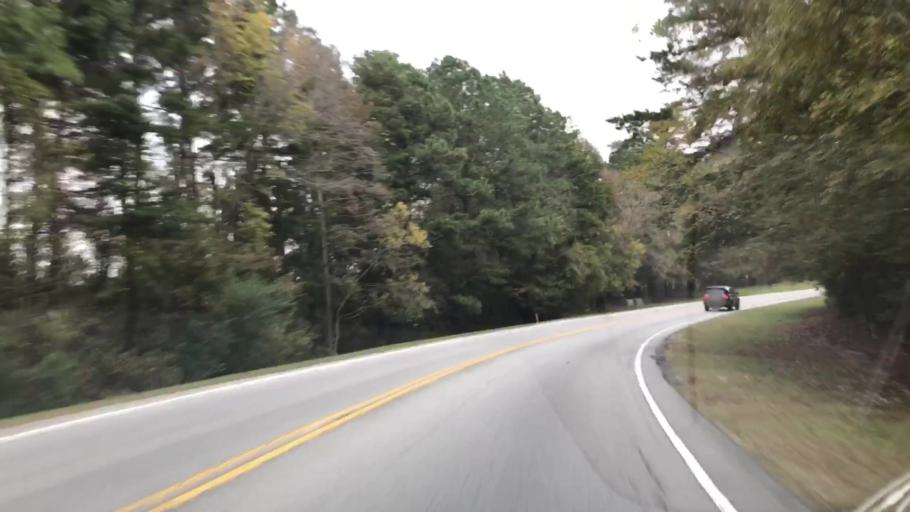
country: US
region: South Carolina
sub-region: Berkeley County
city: Ladson
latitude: 33.0197
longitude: -80.0778
